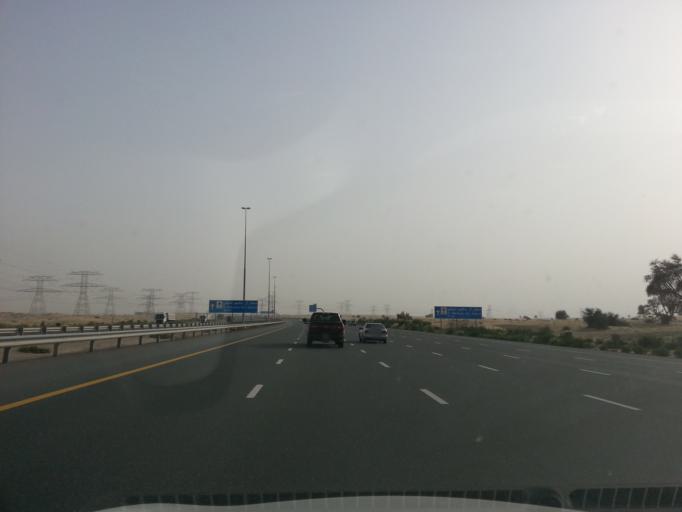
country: AE
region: Dubai
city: Dubai
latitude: 24.9931
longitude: 55.2500
